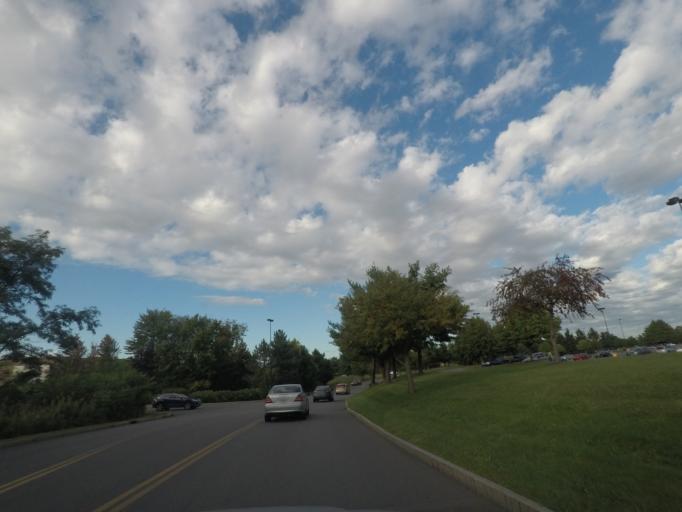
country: US
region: New York
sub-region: Albany County
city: Cohoes
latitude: 42.7540
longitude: -73.7654
